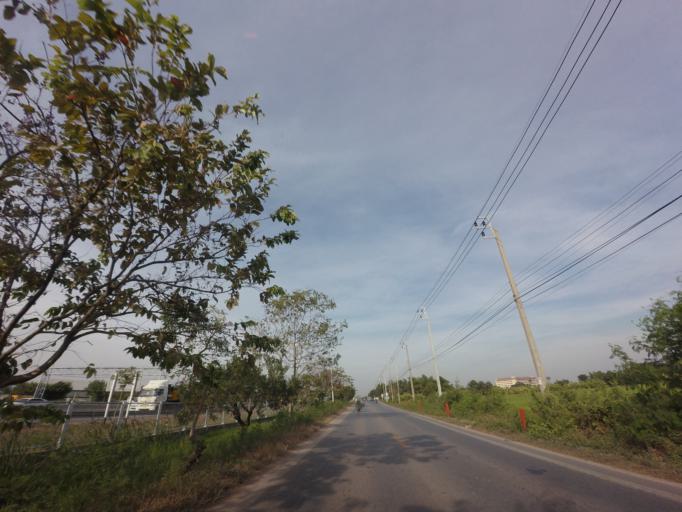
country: TH
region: Bangkok
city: Sai Mai
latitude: 13.8860
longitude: 100.6878
